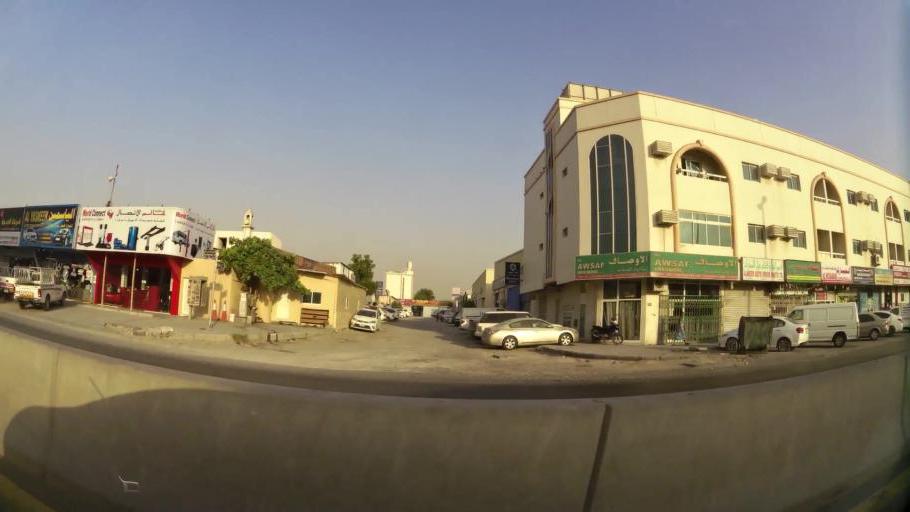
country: AE
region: Ash Shariqah
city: Sharjah
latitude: 25.3199
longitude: 55.4013
